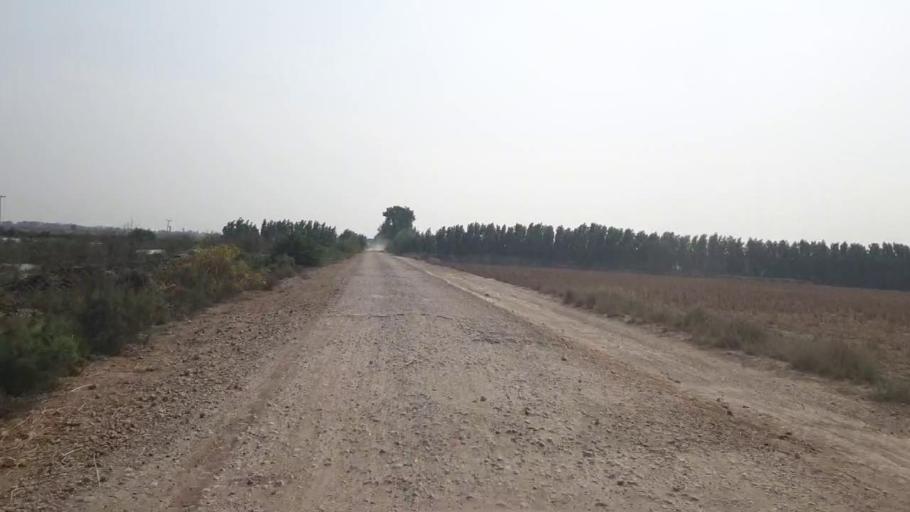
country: PK
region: Sindh
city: Tando Muhammad Khan
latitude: 25.0439
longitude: 68.3905
